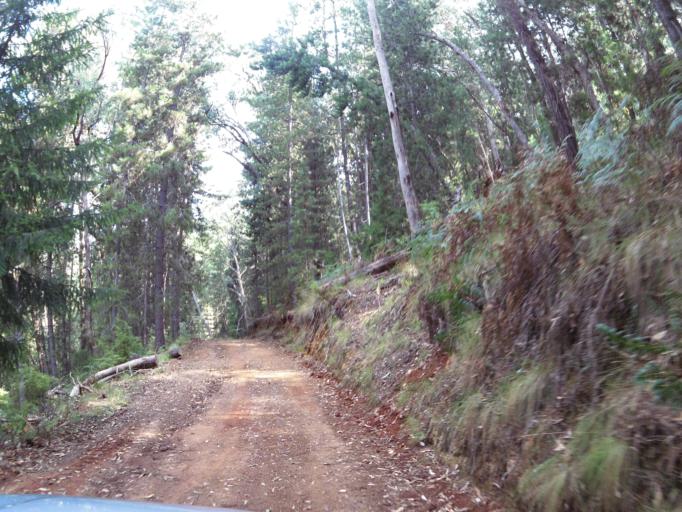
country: AU
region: Victoria
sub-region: Alpine
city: Mount Beauty
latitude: -36.7694
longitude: 147.0155
